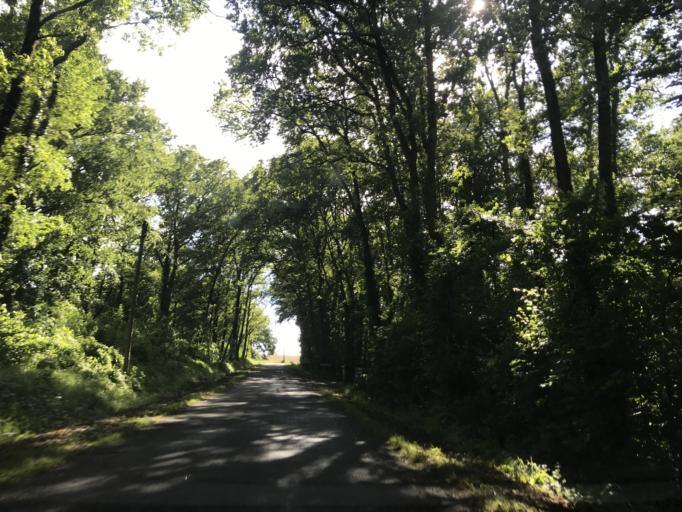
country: FR
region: Poitou-Charentes
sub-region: Departement de la Charente
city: Chalais
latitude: 45.2745
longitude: -0.0165
